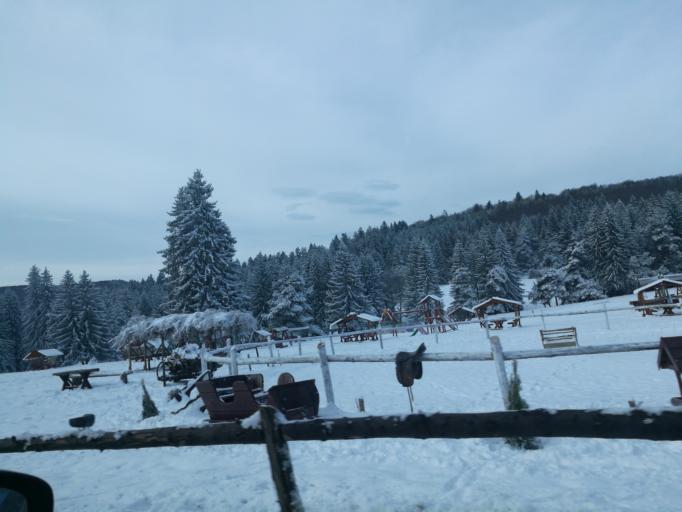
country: RO
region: Brasov
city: Brasov
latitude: 45.6153
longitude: 25.5468
